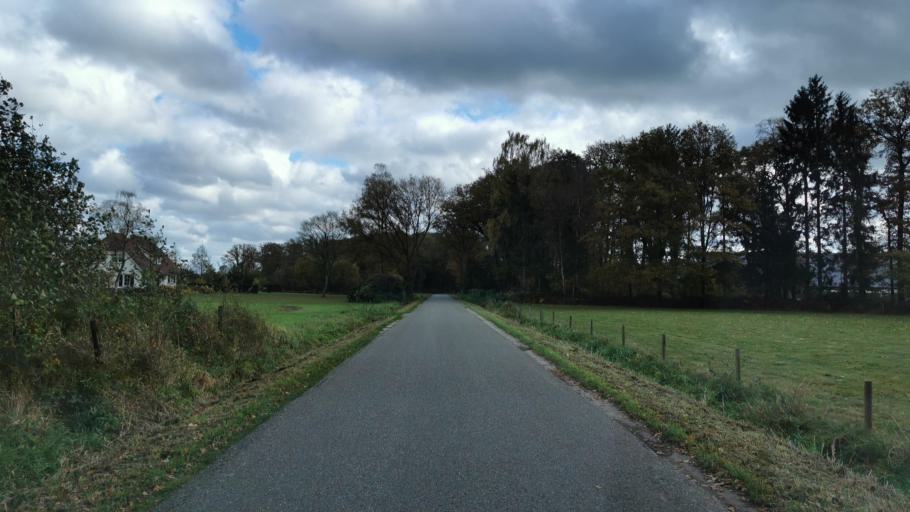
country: NL
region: Overijssel
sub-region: Gemeente Enschede
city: Enschede
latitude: 52.1962
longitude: 6.9359
